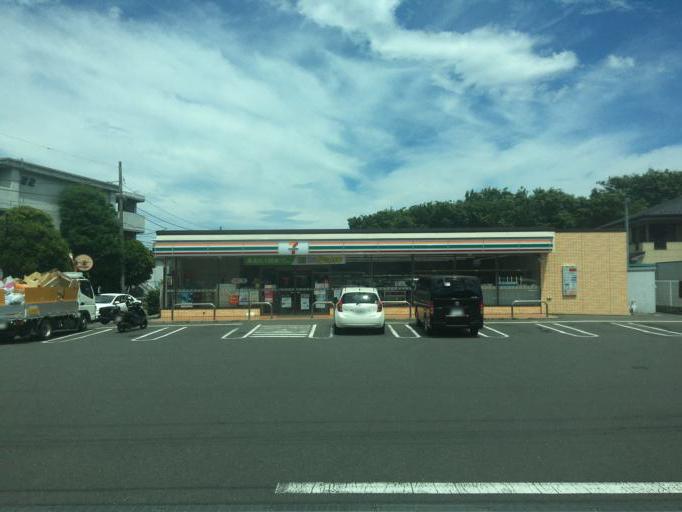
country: JP
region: Tokyo
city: Higashimurayama-shi
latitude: 35.7532
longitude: 139.4797
